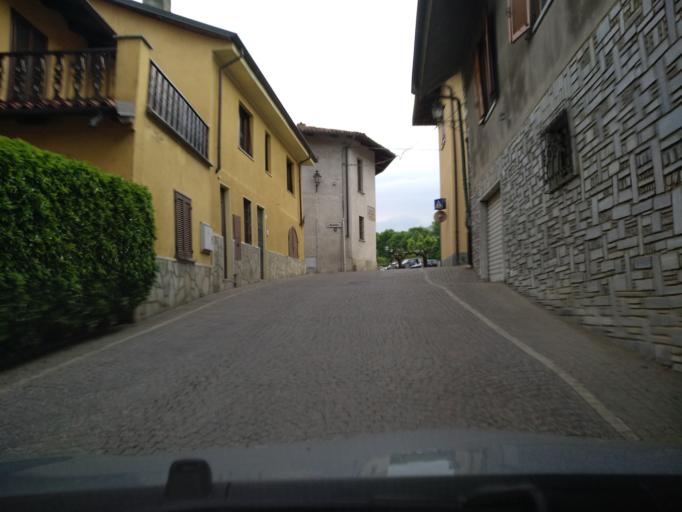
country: IT
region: Piedmont
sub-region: Provincia di Torino
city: Roletto
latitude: 44.9254
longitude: 7.3315
